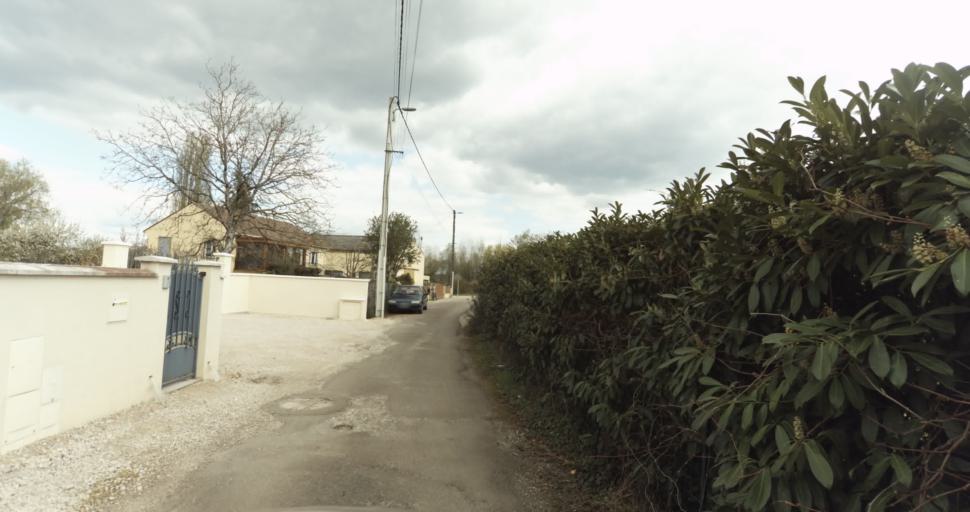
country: FR
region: Bourgogne
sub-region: Departement de la Cote-d'Or
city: Auxonne
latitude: 47.1916
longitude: 5.3939
